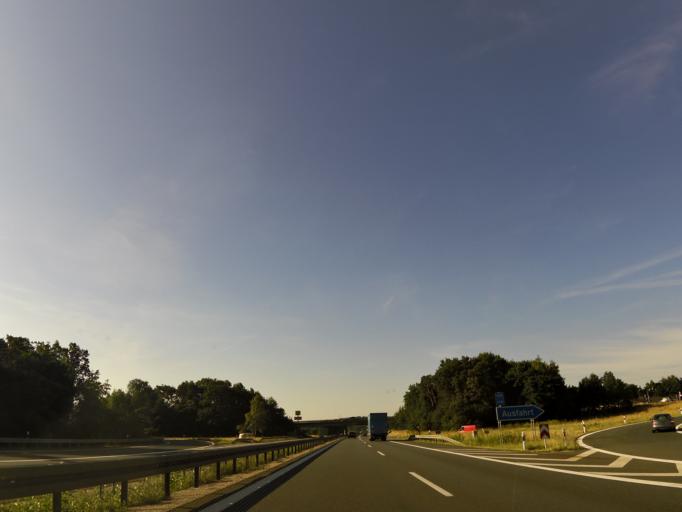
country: DE
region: Bavaria
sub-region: Regierungsbezirk Mittelfranken
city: Hessdorf
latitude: 49.6306
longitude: 10.9177
